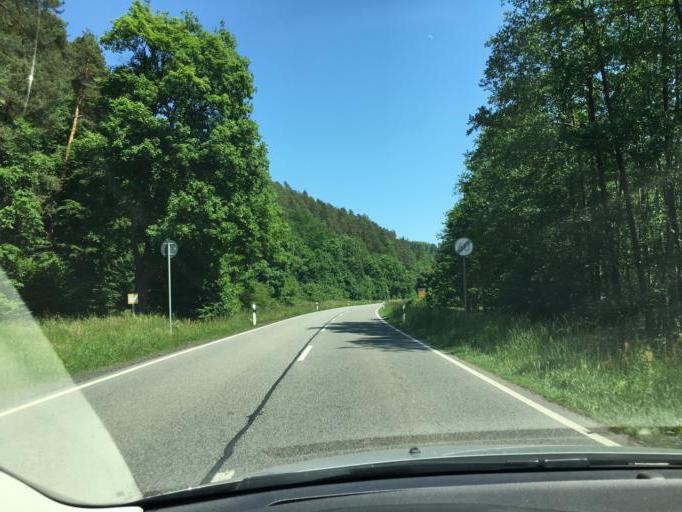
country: DE
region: Hesse
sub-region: Regierungsbezirk Kassel
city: Ronshausen
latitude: 50.9444
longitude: 9.8839
